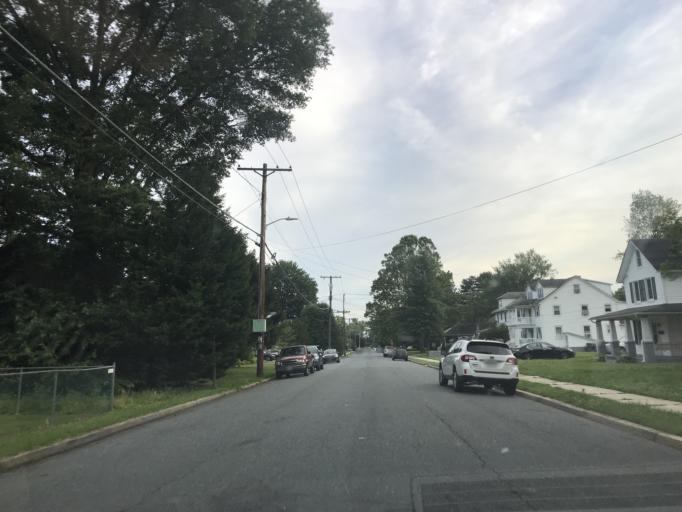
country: US
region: Maryland
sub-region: Harford County
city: Aberdeen
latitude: 39.5072
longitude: -76.1672
